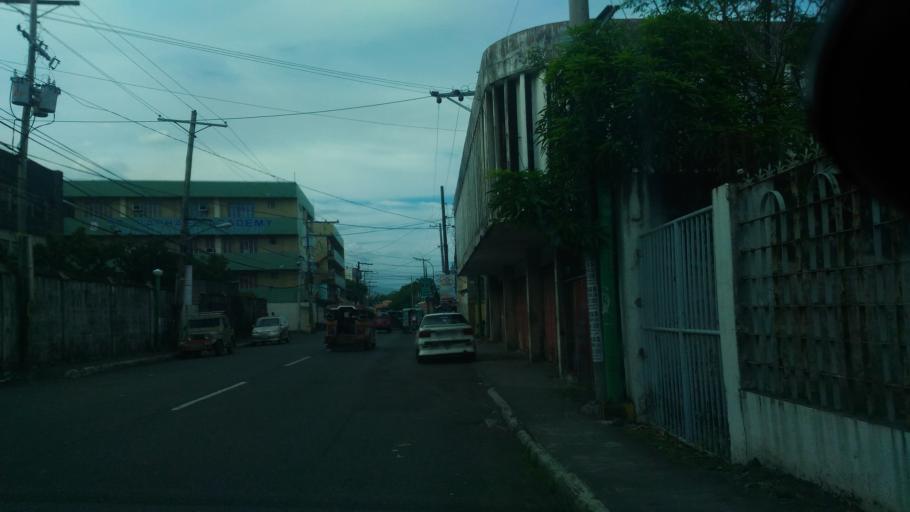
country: PH
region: Bicol
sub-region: Province of Albay
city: San Roque
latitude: 13.1484
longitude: 123.7549
